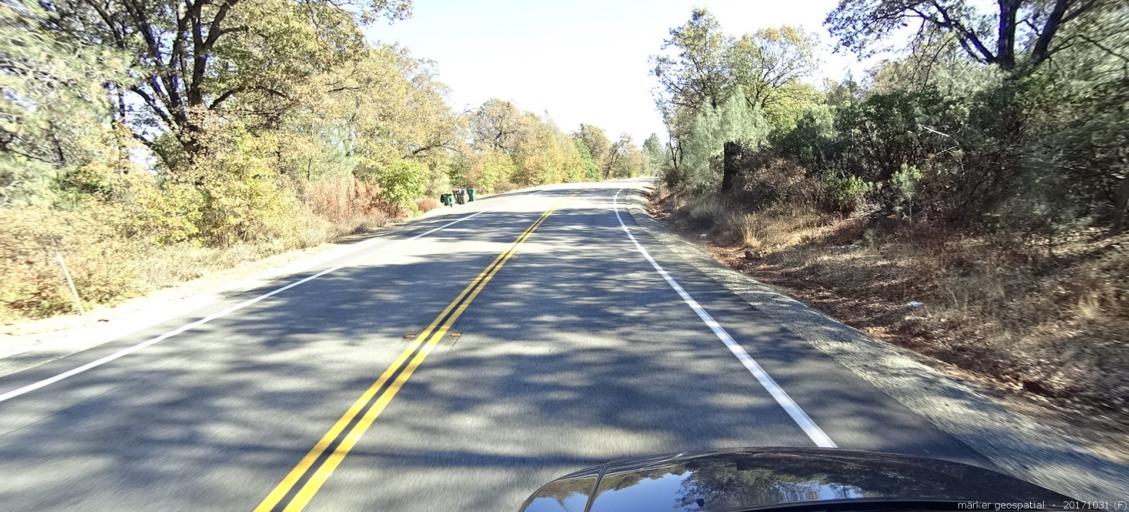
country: US
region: California
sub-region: Shasta County
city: Shingletown
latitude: 40.5098
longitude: -122.0139
